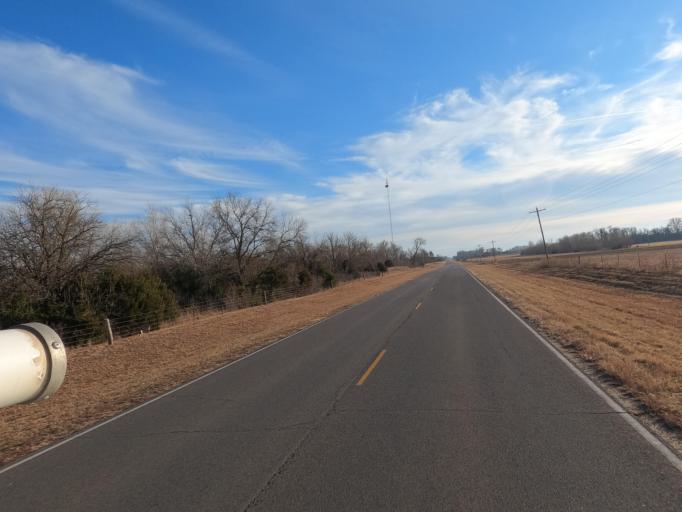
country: US
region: Kansas
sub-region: Reno County
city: Buhler
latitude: 38.1033
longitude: -97.7755
